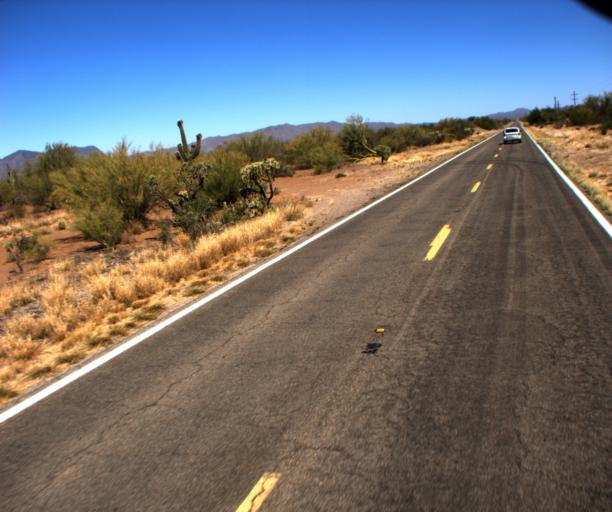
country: US
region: Arizona
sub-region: Pima County
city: Sells
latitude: 32.0401
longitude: -112.0173
